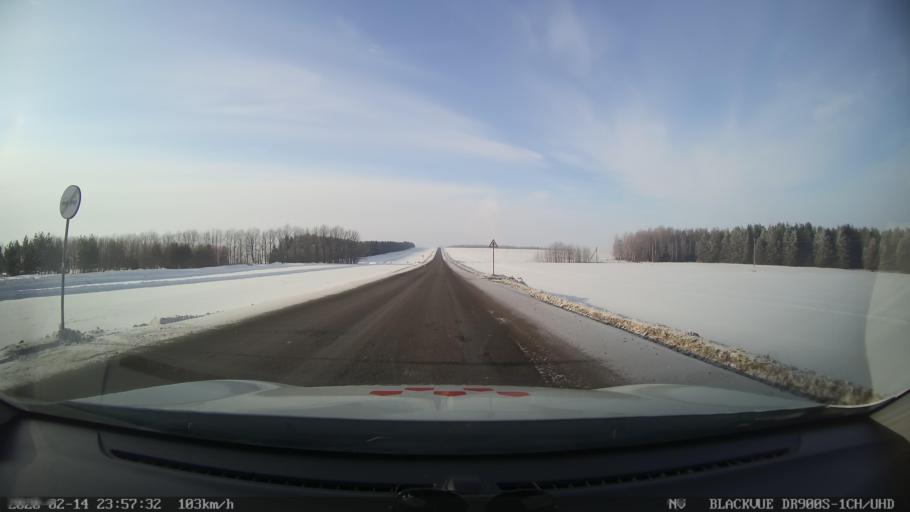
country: RU
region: Tatarstan
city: Kuybyshevskiy Zaton
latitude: 55.3347
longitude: 49.1069
